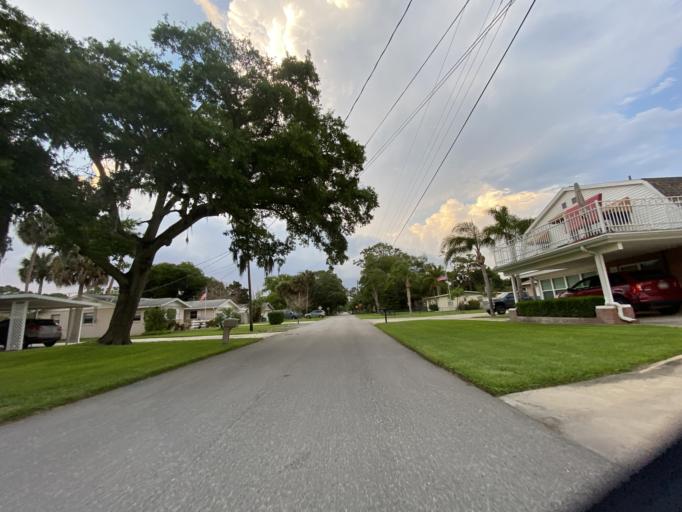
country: US
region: Florida
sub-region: Volusia County
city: Port Orange
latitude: 29.1456
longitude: -80.9965
